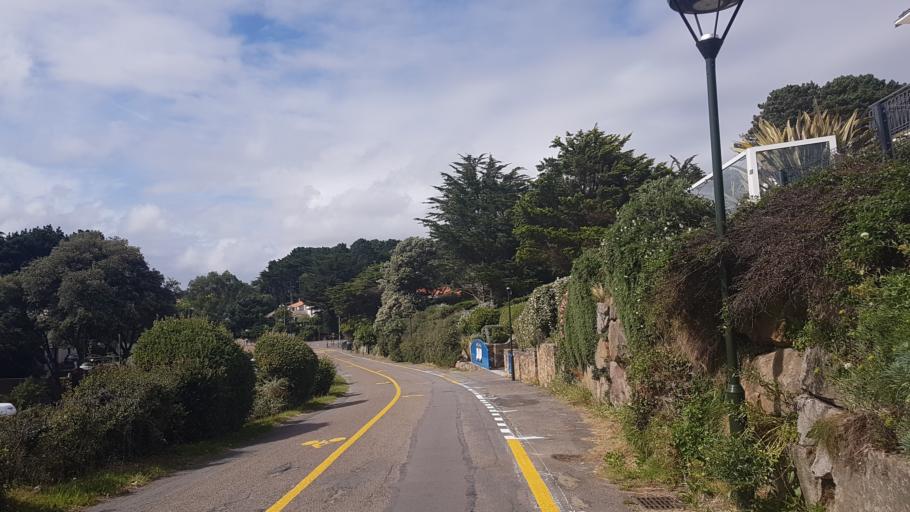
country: FR
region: Pays de la Loire
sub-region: Departement de la Loire-Atlantique
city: La Plaine-sur-Mer
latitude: 47.1136
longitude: -2.1464
